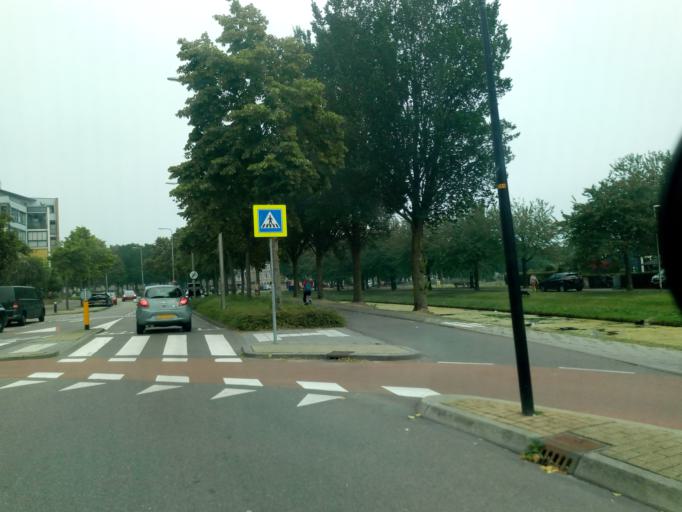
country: NL
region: South Holland
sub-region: Gemeente Alphen aan den Rijn
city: Alphen aan den Rijn
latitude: 52.1235
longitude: 4.6514
